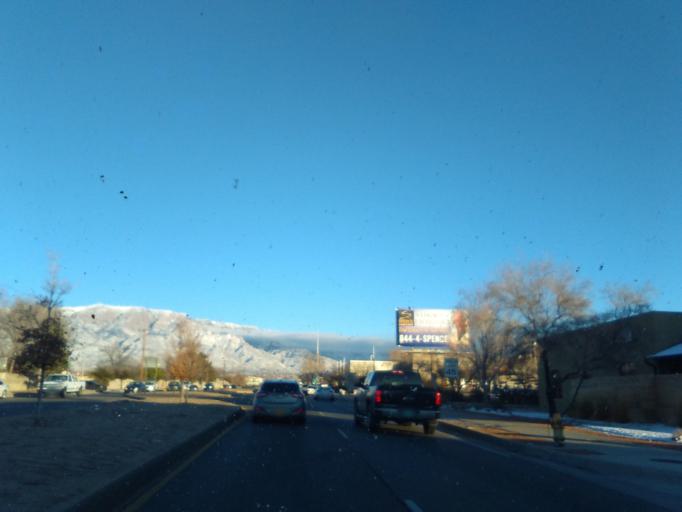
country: US
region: New Mexico
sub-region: Bernalillo County
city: North Valley
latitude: 35.1845
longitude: -106.5907
